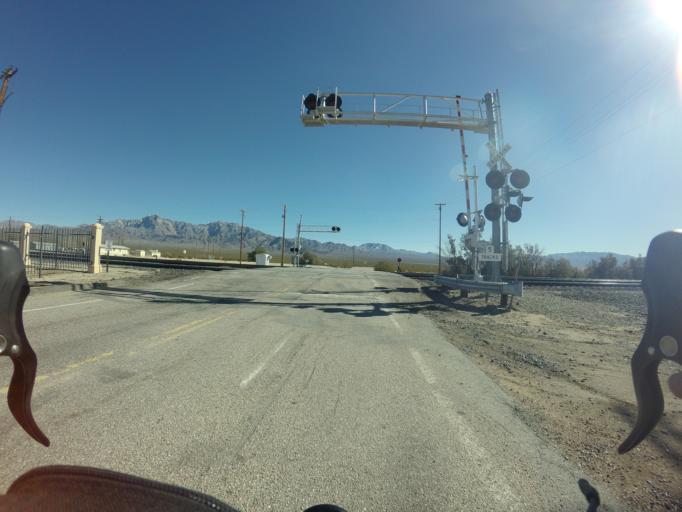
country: US
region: Nevada
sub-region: Clark County
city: Sandy Valley
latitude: 35.0117
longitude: -115.6540
